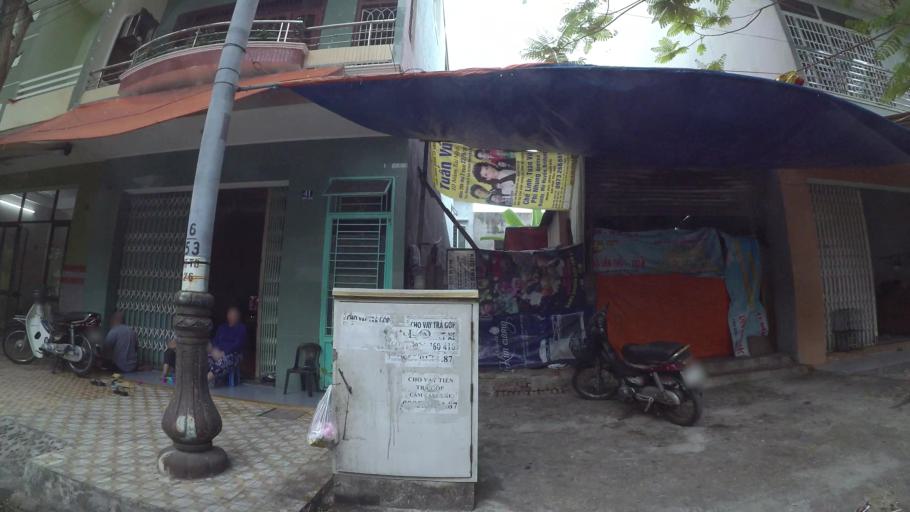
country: VN
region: Da Nang
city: Son Tra
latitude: 16.0536
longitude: 108.2349
